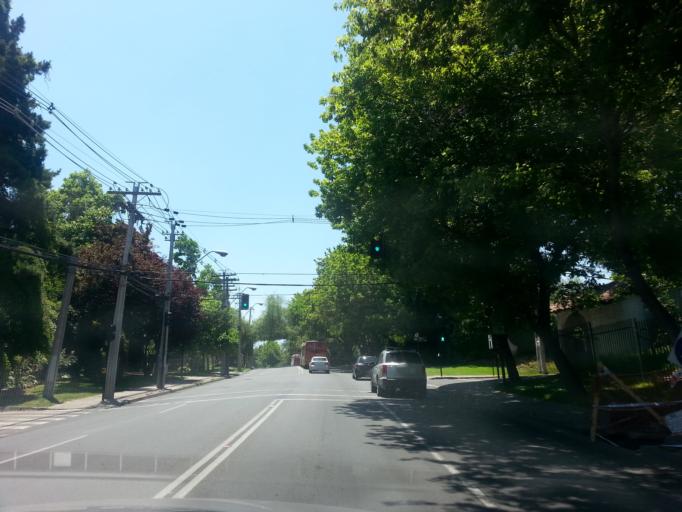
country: CL
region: Santiago Metropolitan
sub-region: Provincia de Santiago
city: Villa Presidente Frei, Nunoa, Santiago, Chile
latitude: -33.4041
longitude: -70.5362
